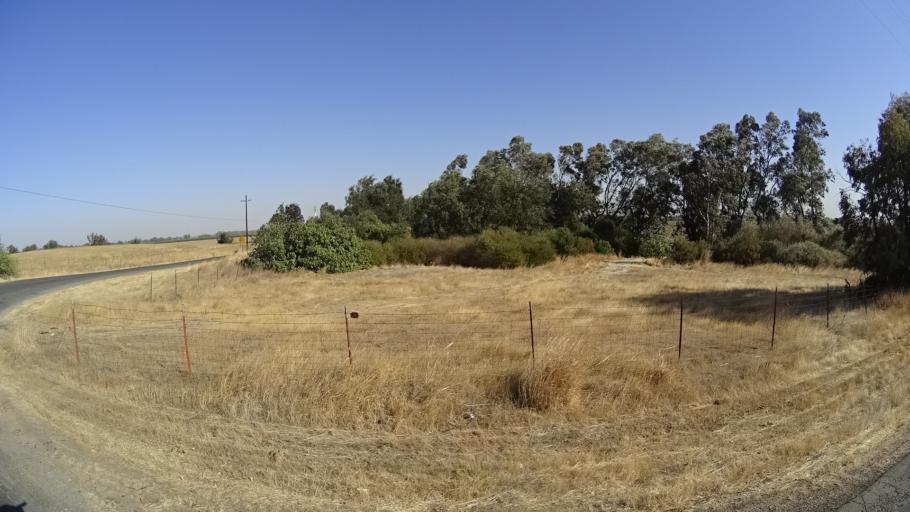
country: US
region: California
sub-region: Yolo County
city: Woodland
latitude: 38.7283
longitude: -121.8562
